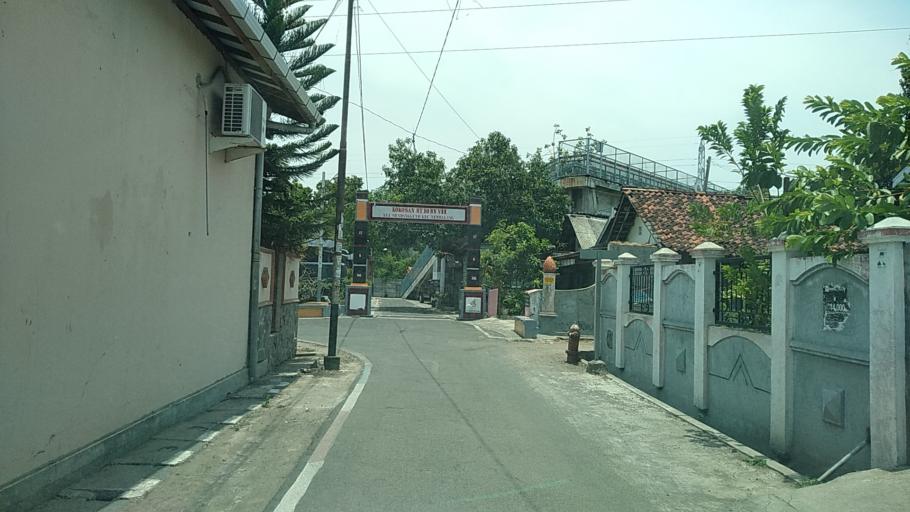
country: ID
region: Central Java
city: Semarang
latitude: -7.0092
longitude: 110.4474
